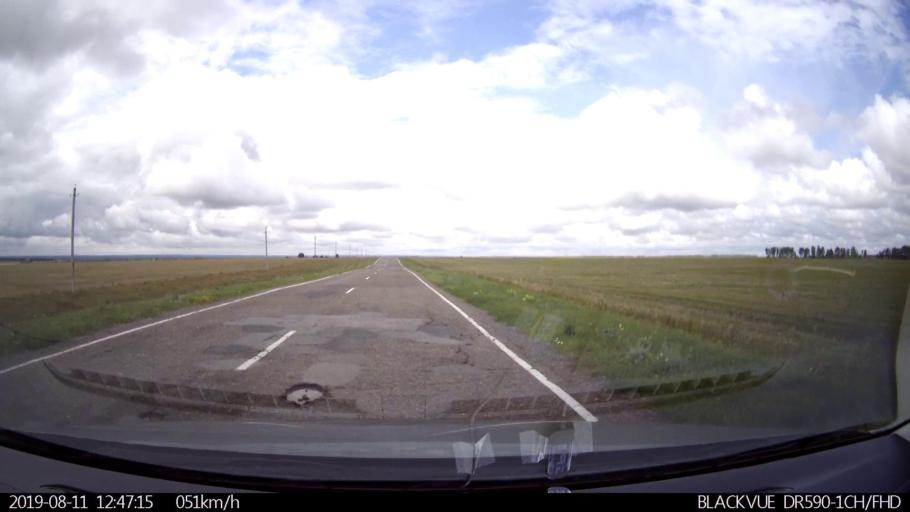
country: RU
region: Ulyanovsk
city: Ignatovka
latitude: 53.8686
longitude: 47.7104
